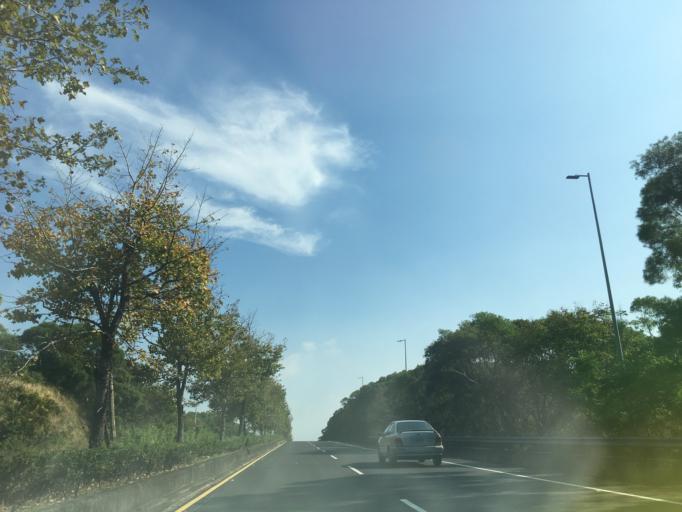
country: TW
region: Taiwan
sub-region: Hsinchu
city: Hsinchu
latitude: 24.7689
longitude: 120.9529
